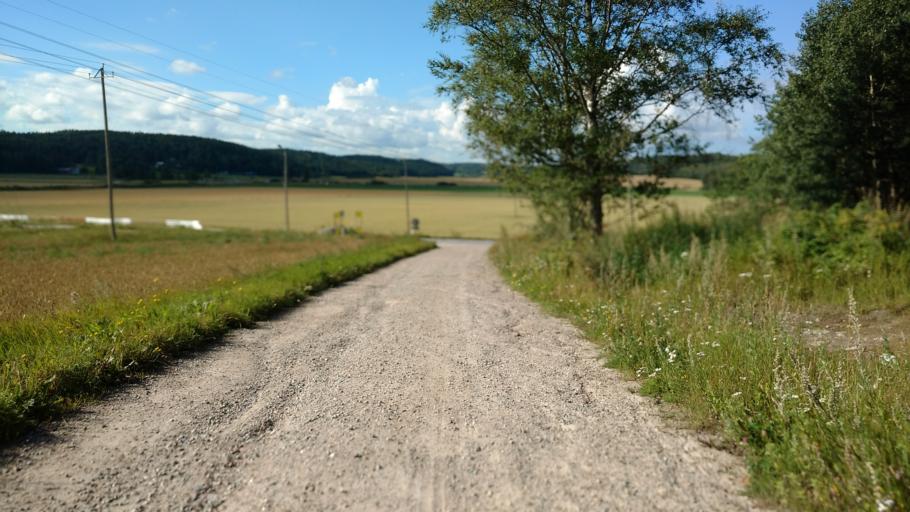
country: FI
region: Varsinais-Suomi
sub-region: Salo
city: Salo
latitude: 60.3758
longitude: 23.1670
